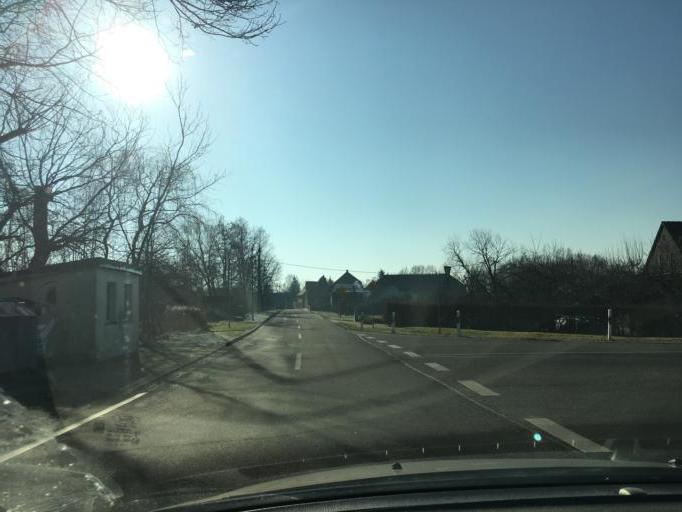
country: DE
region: Saxony
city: Belgershain
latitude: 51.2167
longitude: 12.5577
